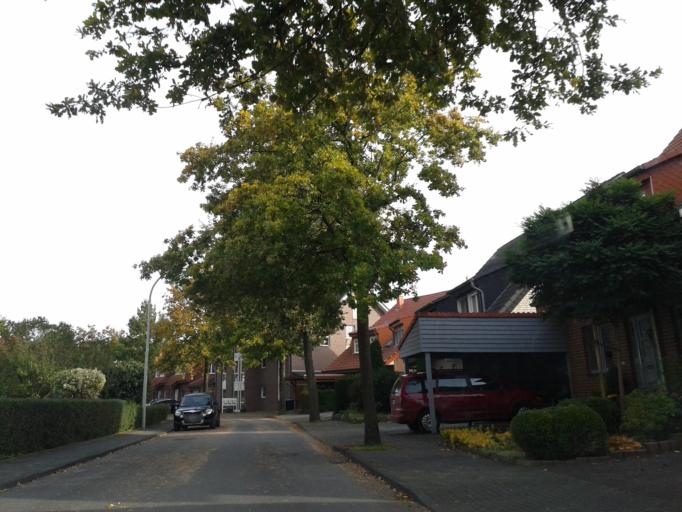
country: DE
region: North Rhine-Westphalia
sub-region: Regierungsbezirk Detmold
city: Paderborn
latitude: 51.7280
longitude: 8.6819
